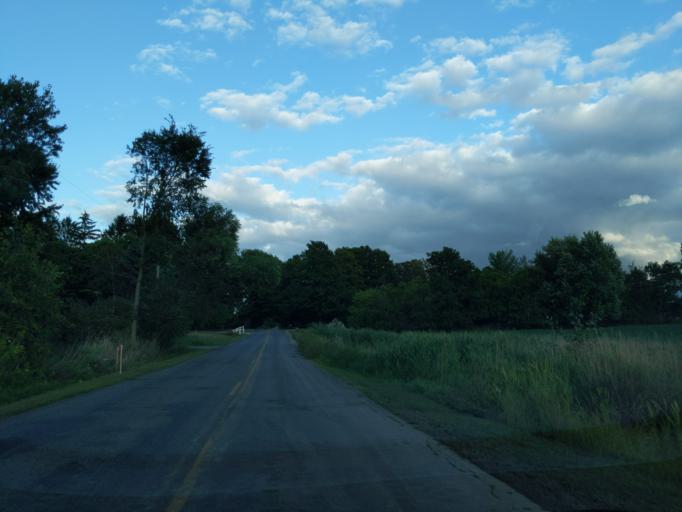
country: US
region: Michigan
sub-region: Ingham County
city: Holt
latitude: 42.5967
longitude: -84.5384
